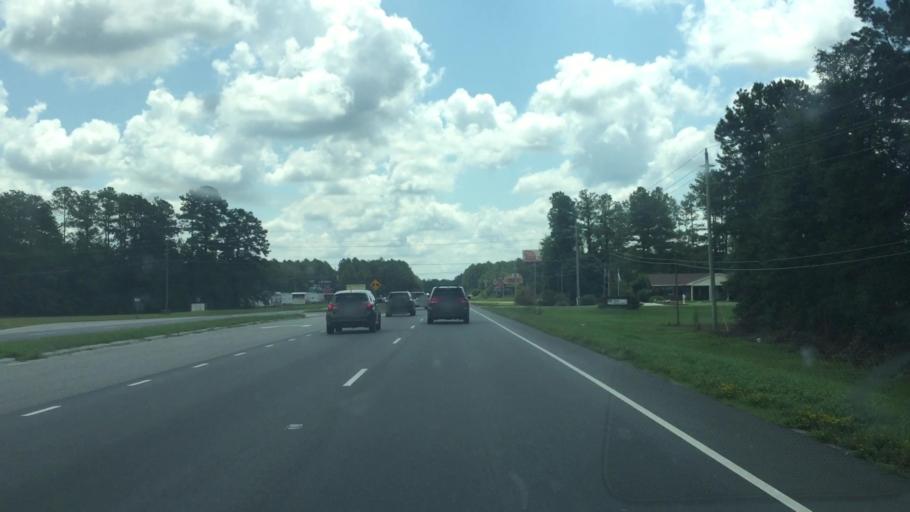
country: US
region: North Carolina
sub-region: Scotland County
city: Laurel Hill
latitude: 34.8056
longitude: -79.5425
